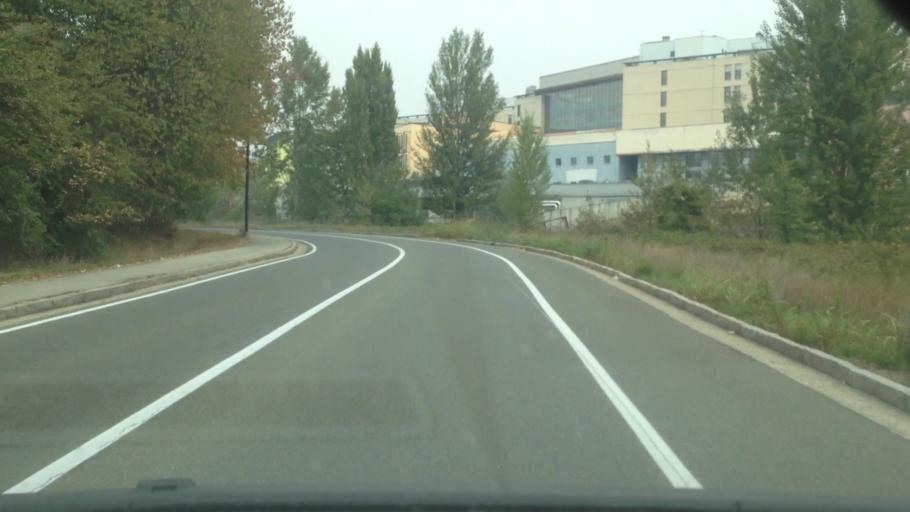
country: IT
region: Piedmont
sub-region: Provincia di Asti
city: Asti
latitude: 44.9105
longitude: 8.1923
